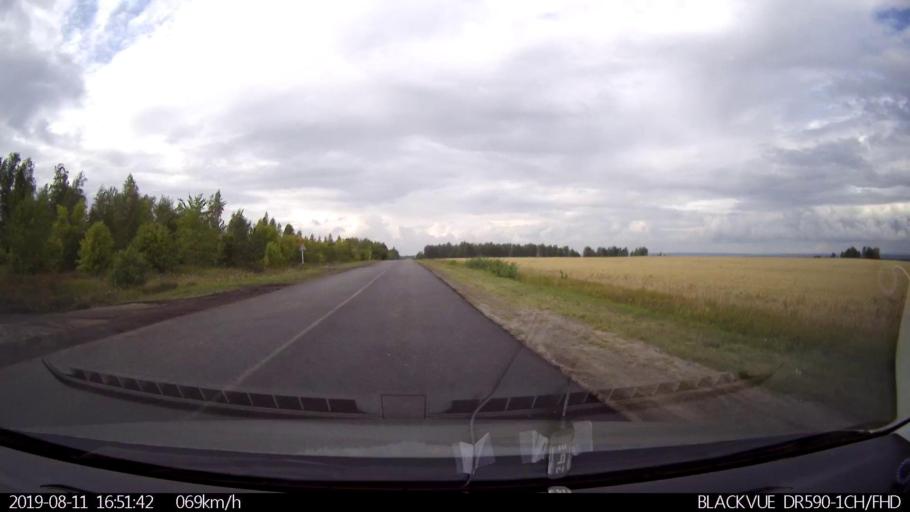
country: RU
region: Ulyanovsk
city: Mayna
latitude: 54.2399
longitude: 47.6762
